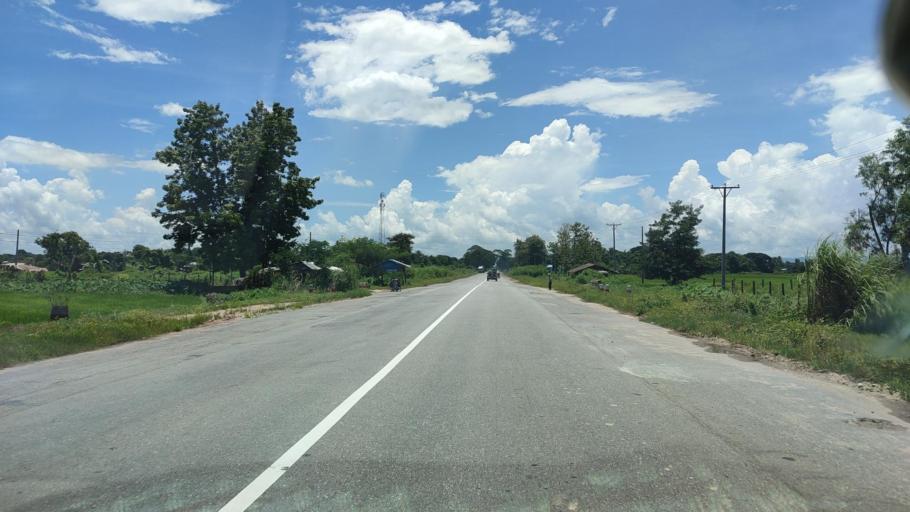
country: MM
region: Bago
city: Taungoo
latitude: 18.7273
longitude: 96.4074
